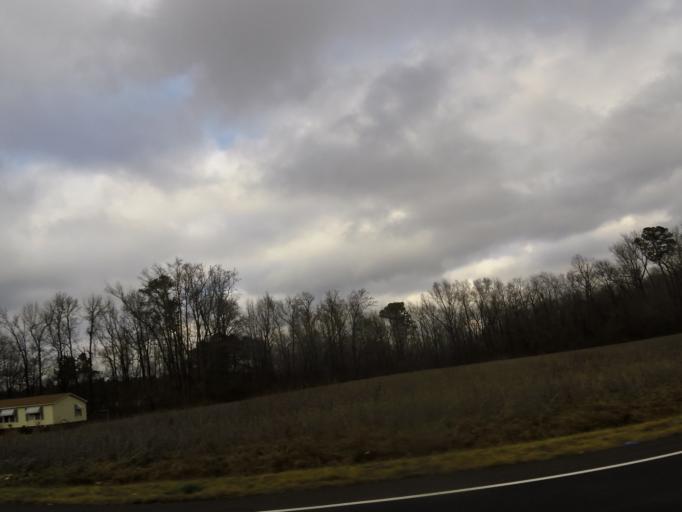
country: US
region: North Carolina
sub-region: Nash County
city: Rocky Mount
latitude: 35.8714
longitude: -77.7382
